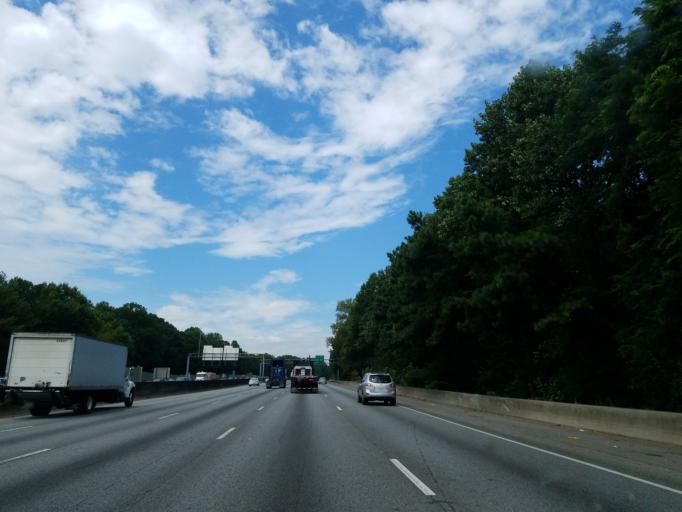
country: US
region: Georgia
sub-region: Fulton County
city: Sandy Springs
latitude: 33.9144
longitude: -84.3931
